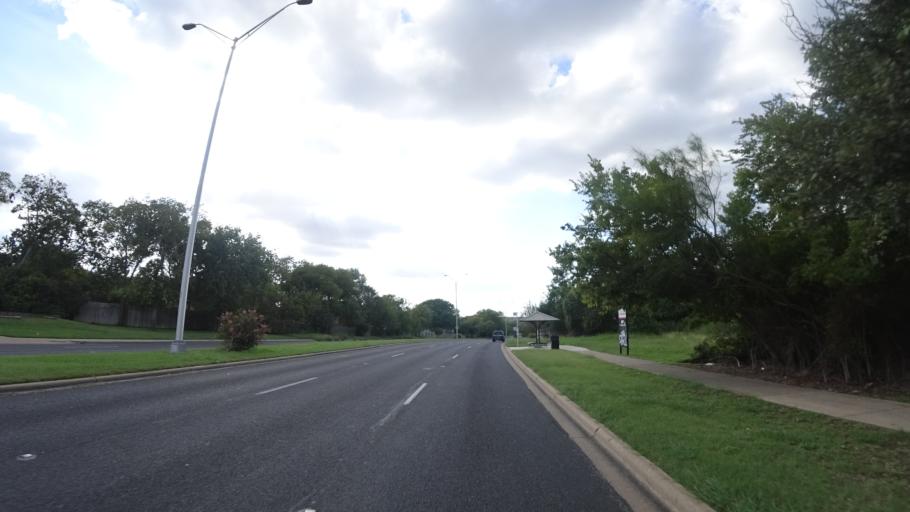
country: US
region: Texas
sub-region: Travis County
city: Onion Creek
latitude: 30.1995
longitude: -97.7953
